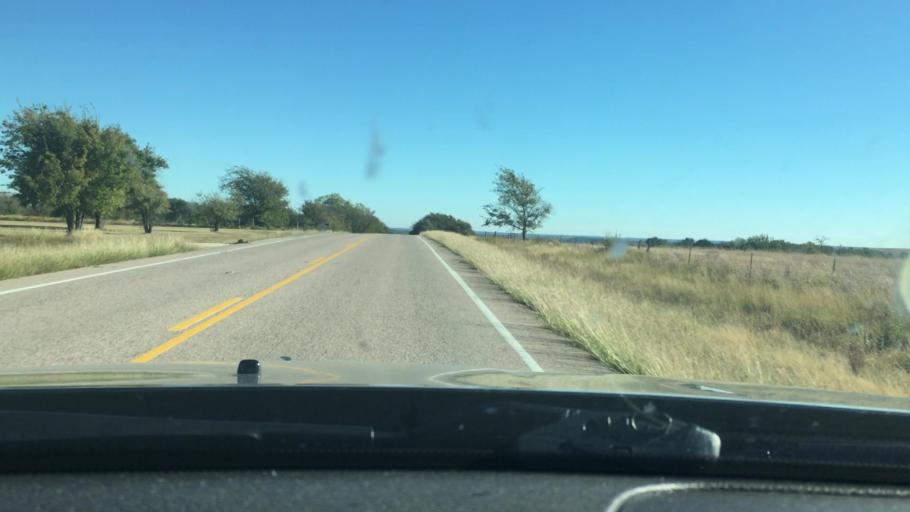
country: US
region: Oklahoma
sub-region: Marshall County
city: Madill
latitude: 34.1347
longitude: -96.7171
